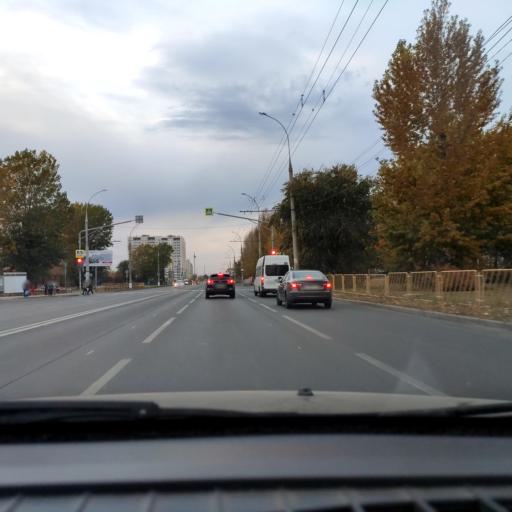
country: RU
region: Samara
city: Tol'yatti
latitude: 53.5081
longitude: 49.2609
